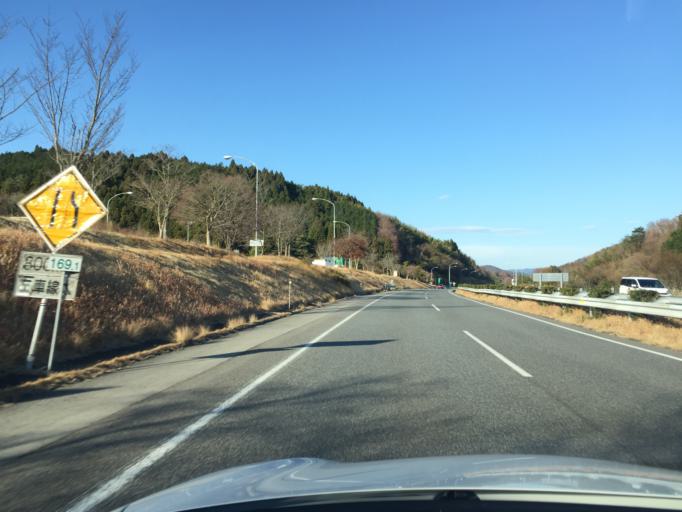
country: JP
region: Fukushima
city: Iwaki
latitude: 37.0189
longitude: 140.8131
